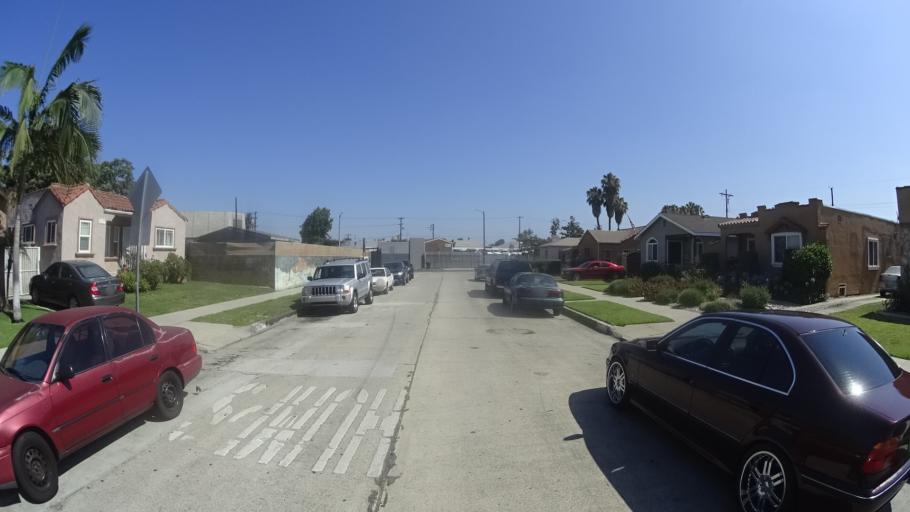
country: US
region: California
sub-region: Los Angeles County
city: View Park-Windsor Hills
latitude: 33.9814
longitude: -118.3206
